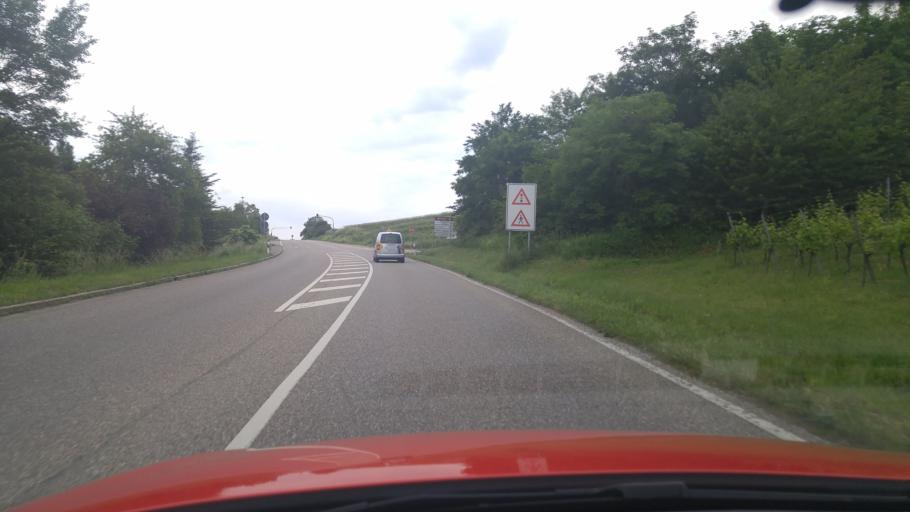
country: DE
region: Baden-Wuerttemberg
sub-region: Regierungsbezirk Stuttgart
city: Erlenbach
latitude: 49.1544
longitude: 9.2523
